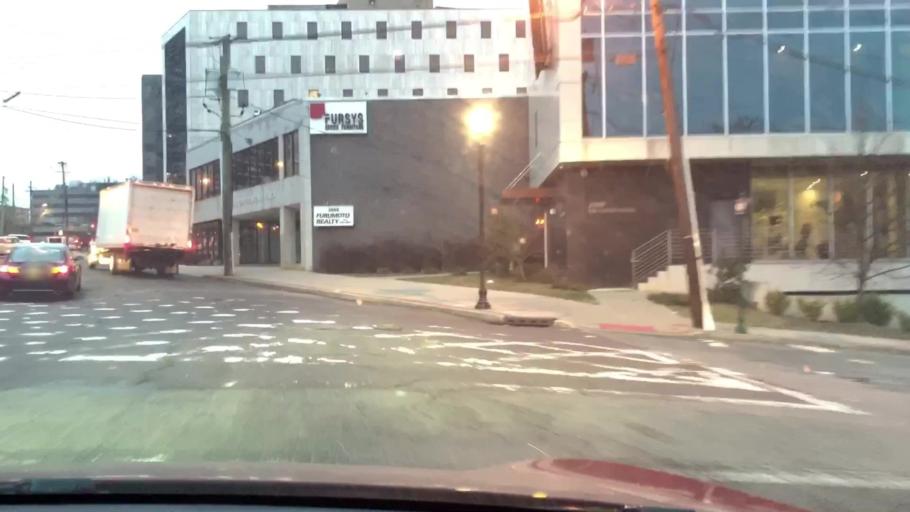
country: US
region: New Jersey
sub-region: Bergen County
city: Fort Lee
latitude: 40.8529
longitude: -73.9715
